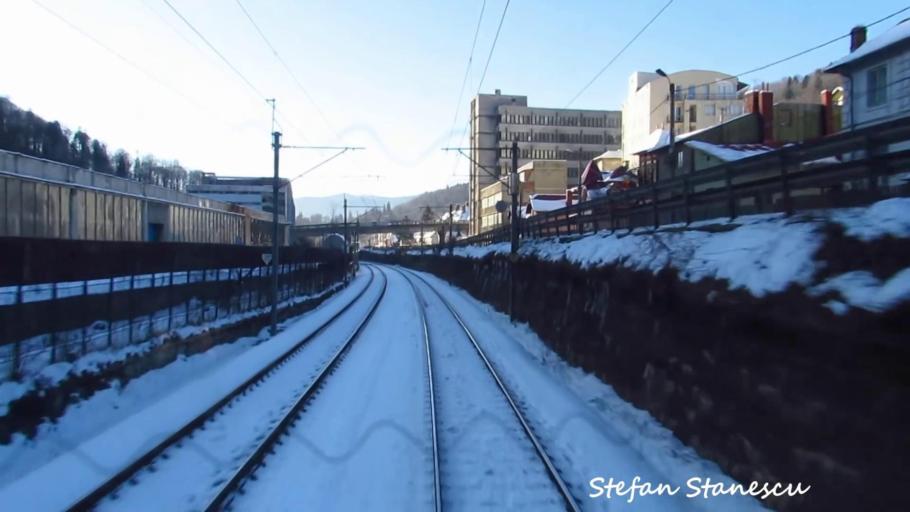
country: RO
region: Prahova
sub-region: Oras Sinaia
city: Sinaia
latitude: 45.3428
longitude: 25.5510
